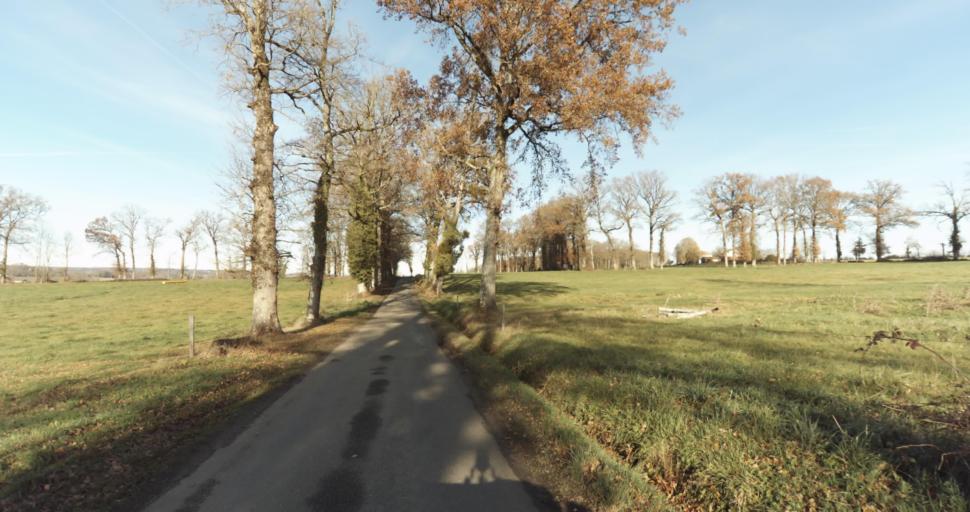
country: FR
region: Limousin
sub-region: Departement de la Haute-Vienne
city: Aixe-sur-Vienne
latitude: 45.7862
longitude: 1.1156
